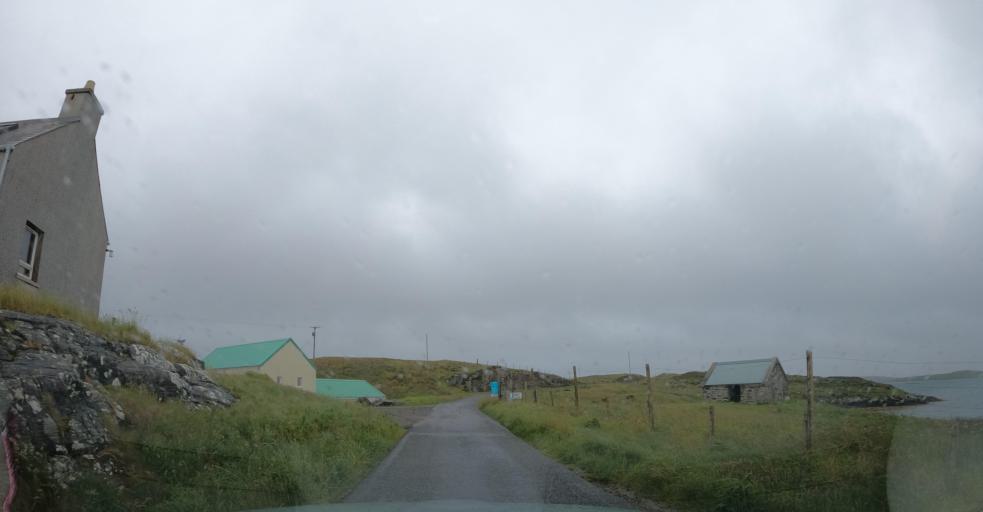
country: GB
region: Scotland
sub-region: Eilean Siar
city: Benbecula
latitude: 57.4846
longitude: -7.2303
